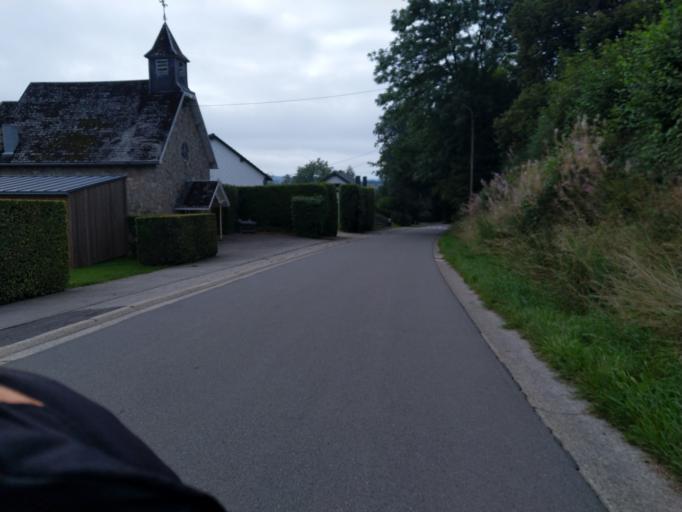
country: BE
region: Wallonia
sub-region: Province de Liege
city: Malmedy
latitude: 50.4555
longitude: 6.0532
